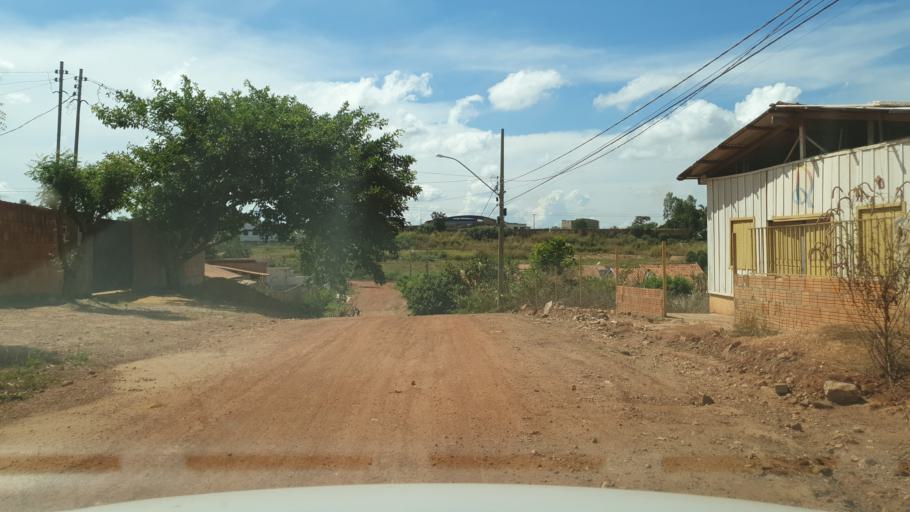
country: BR
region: Mato Grosso
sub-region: Pontes E Lacerda
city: Pontes e Lacerda
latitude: -15.2515
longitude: -59.3142
